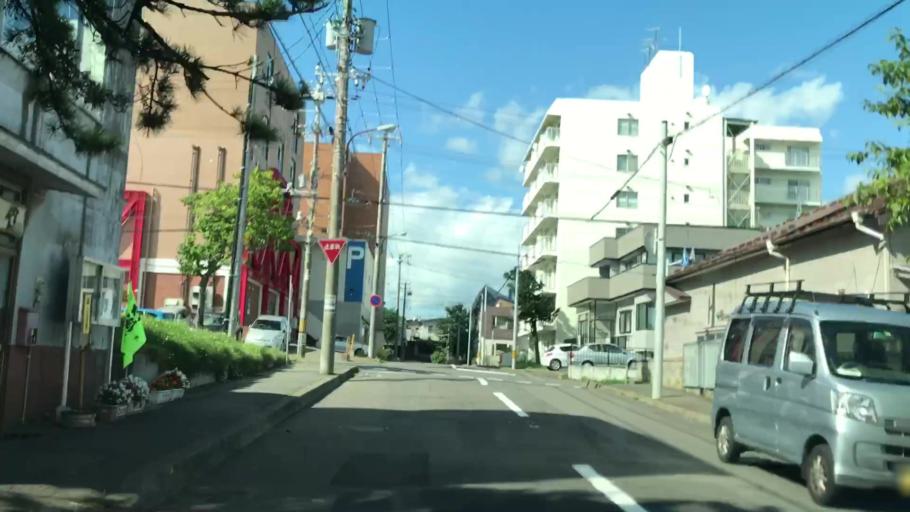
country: JP
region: Hokkaido
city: Muroran
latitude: 42.3149
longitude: 140.9710
